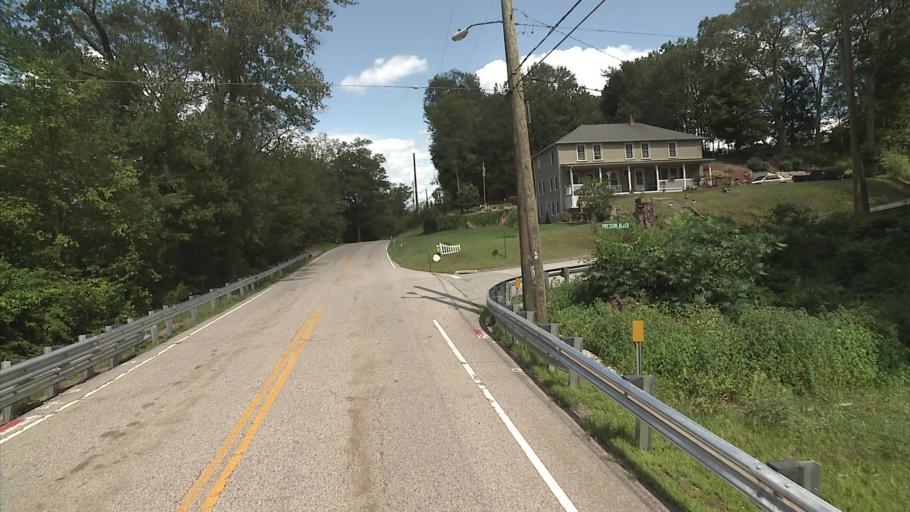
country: US
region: Connecticut
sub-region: New London County
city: Lisbon
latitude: 41.6025
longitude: -72.0420
